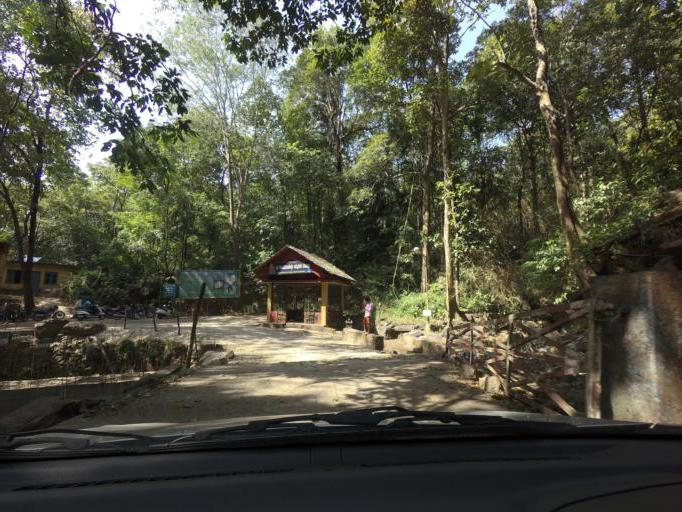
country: IN
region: Karnataka
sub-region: Kodagu
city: Somvarpet
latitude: 12.7011
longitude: 75.6400
